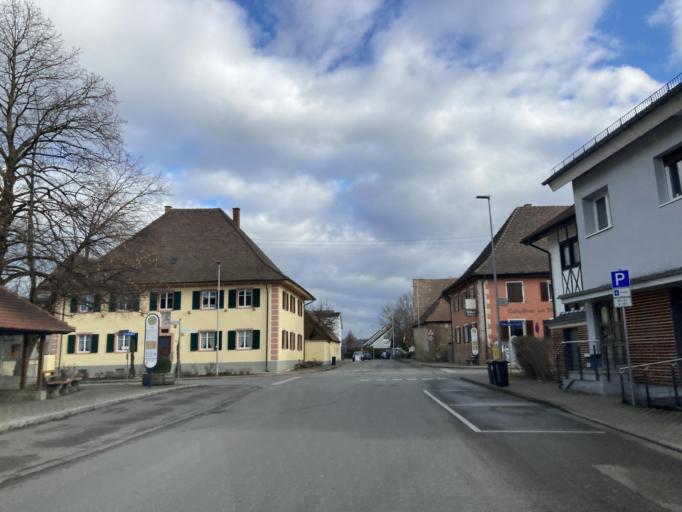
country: DE
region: Baden-Wuerttemberg
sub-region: Freiburg Region
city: Unterkrozingen
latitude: 47.9547
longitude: 7.6713
